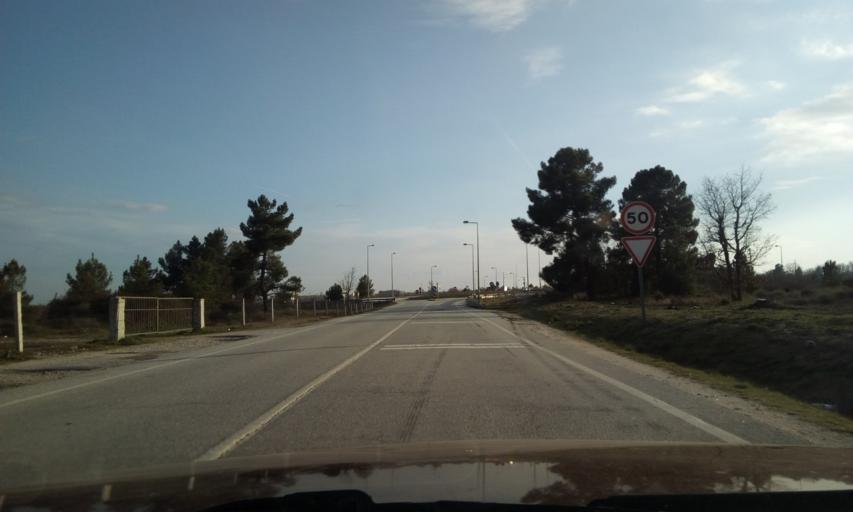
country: ES
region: Castille and Leon
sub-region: Provincia de Salamanca
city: Fuentes de Onoro
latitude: 40.6097
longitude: -6.9825
